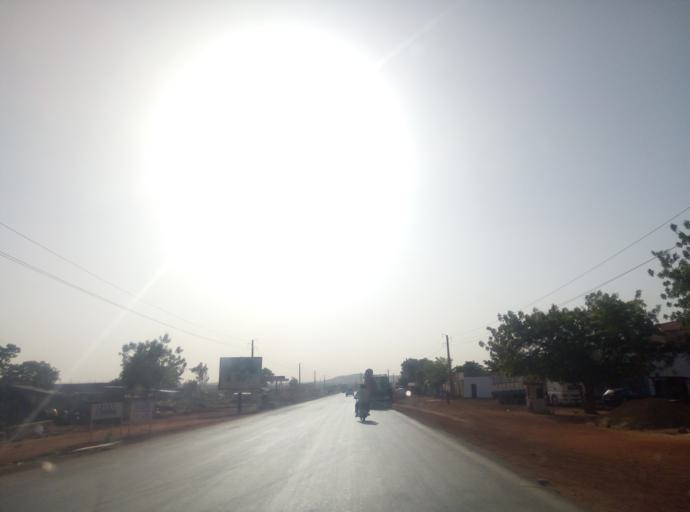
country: ML
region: Bamako
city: Bamako
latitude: 12.5859
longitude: -7.8281
